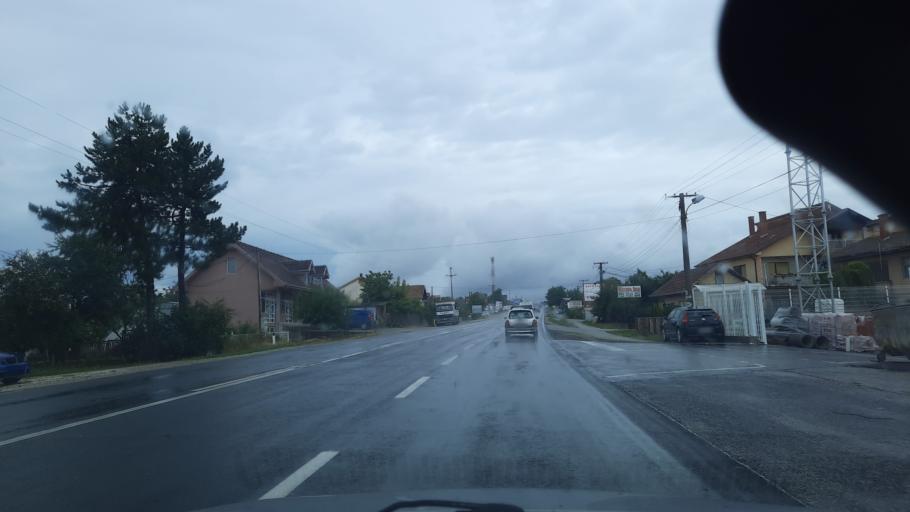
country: RS
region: Central Serbia
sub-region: Sumadijski Okrug
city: Kragujevac
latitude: 43.9904
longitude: 20.8566
